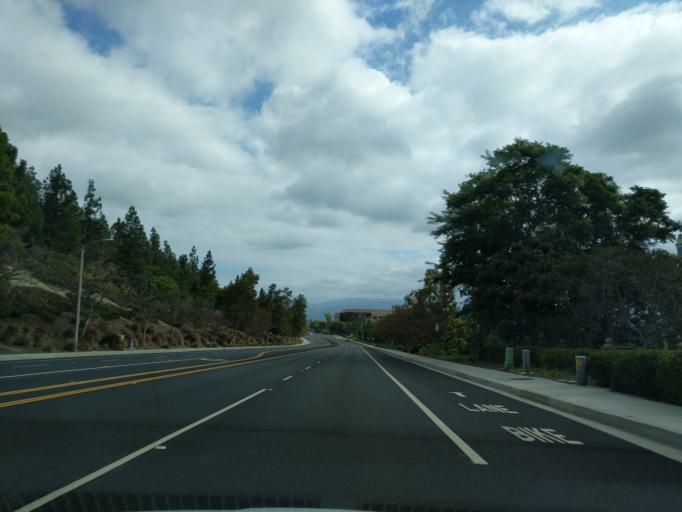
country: US
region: California
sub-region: Orange County
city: Aliso Viejo
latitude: 33.5833
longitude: -117.7372
